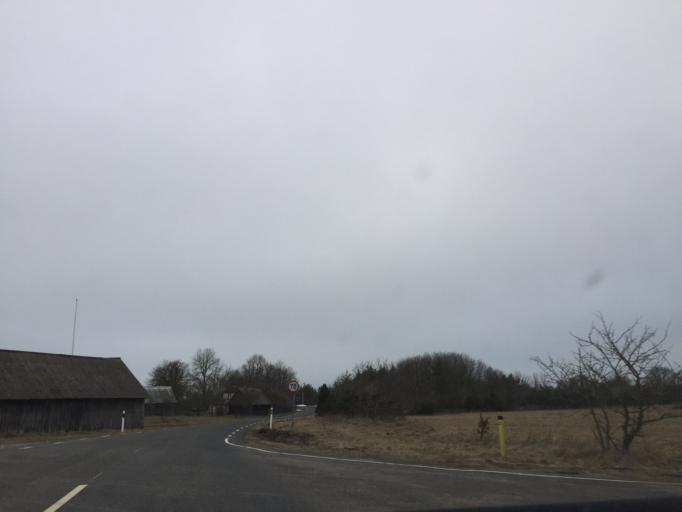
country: EE
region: Saare
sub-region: Kuressaare linn
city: Kuressaare
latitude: 58.5605
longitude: 22.3138
